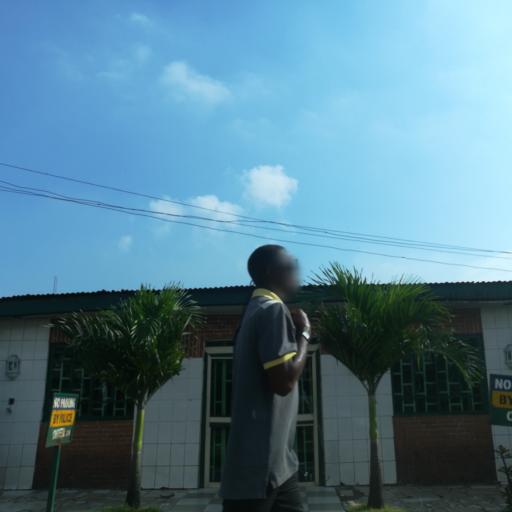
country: NG
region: Rivers
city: Port Harcourt
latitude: 4.8058
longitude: 7.0231
